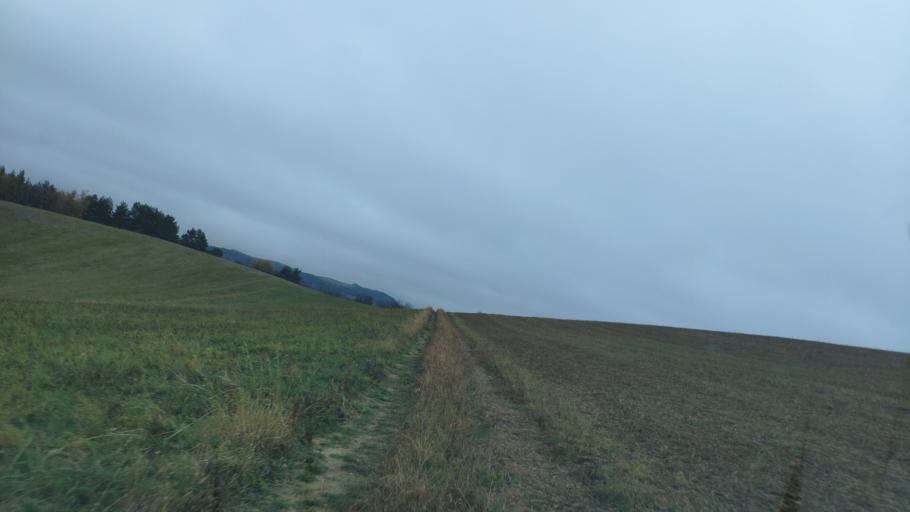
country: SK
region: Presovsky
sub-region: Okres Presov
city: Presov
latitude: 48.9317
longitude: 21.0922
